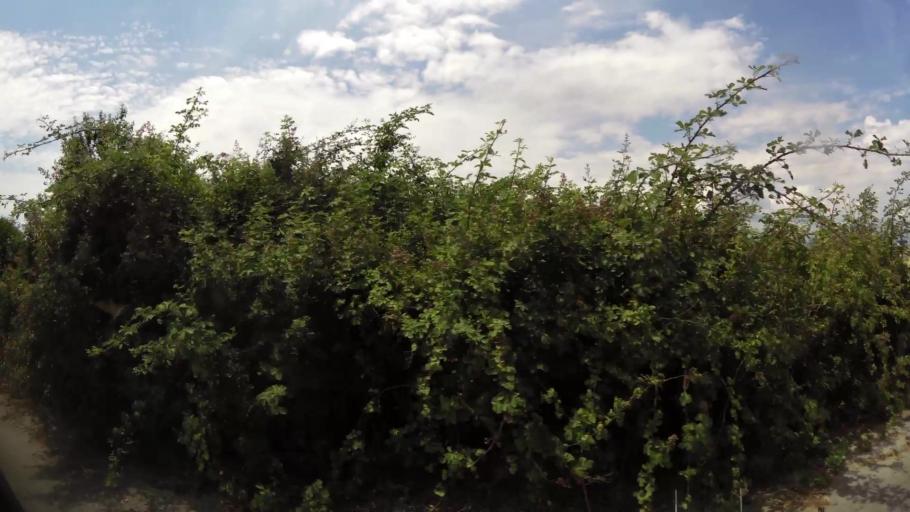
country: GR
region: Central Macedonia
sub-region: Nomos Pierias
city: Katerini
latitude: 40.2612
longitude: 22.5187
